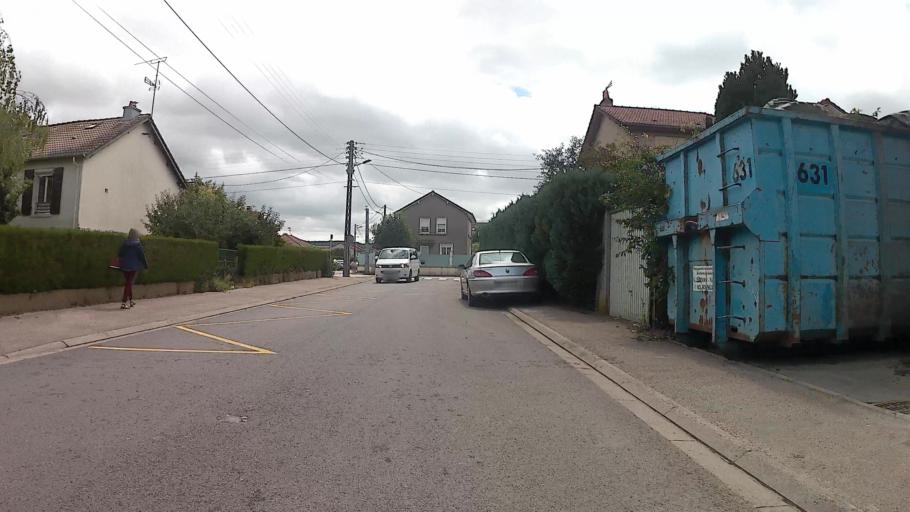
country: FR
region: Lorraine
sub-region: Departement de la Meuse
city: Verdun
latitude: 49.1596
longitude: 5.3967
